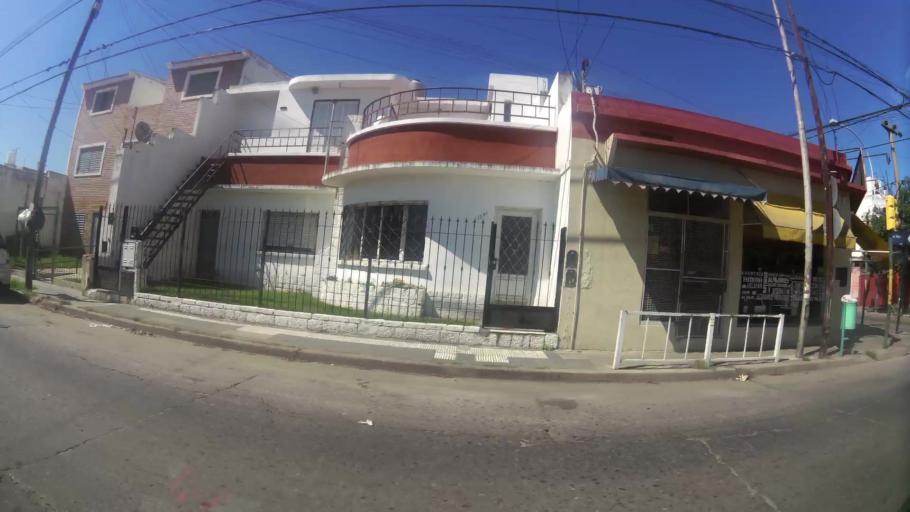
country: AR
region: Cordoba
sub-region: Departamento de Capital
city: Cordoba
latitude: -31.4165
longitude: -64.2103
